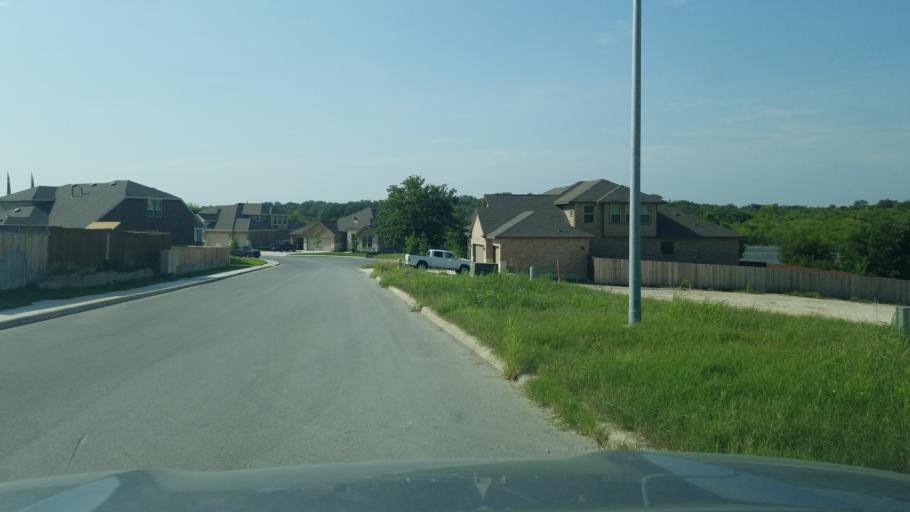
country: US
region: Texas
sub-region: Medina County
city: La Coste
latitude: 29.4030
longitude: -98.7860
